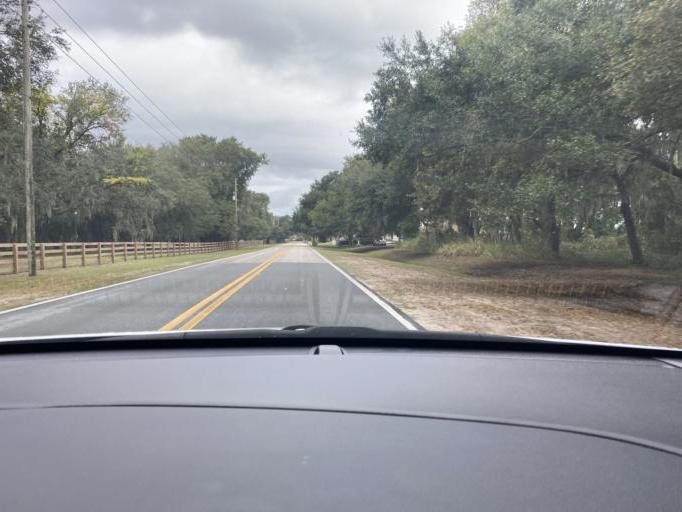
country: US
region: Florida
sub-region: Lake County
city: Clermont
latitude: 28.5722
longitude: -81.7812
